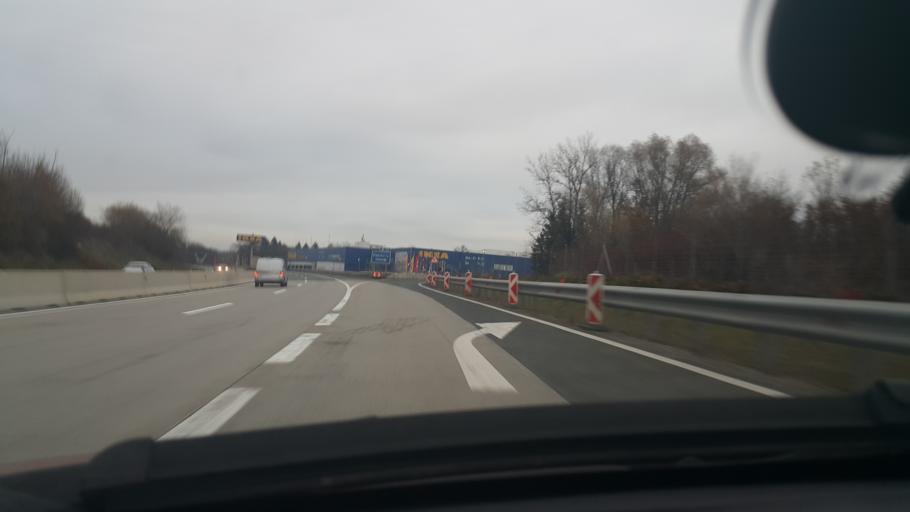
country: AT
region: Carinthia
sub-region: Politischer Bezirk Klagenfurt Land
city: Ebenthal
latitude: 46.6404
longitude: 14.3645
